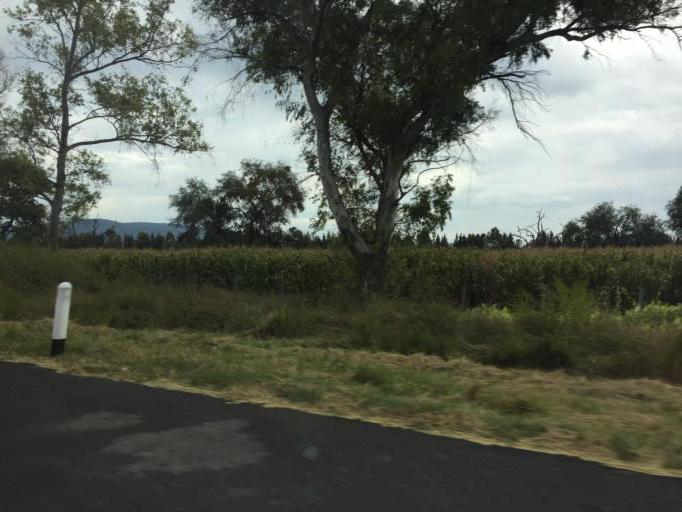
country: MX
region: Jalisco
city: Ocotlan
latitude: 20.3940
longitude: -102.7230
